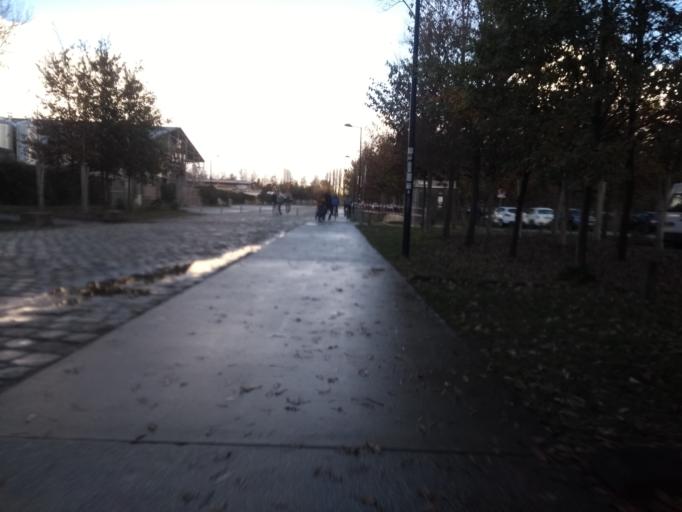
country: FR
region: Aquitaine
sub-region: Departement de la Gironde
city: Bordeaux
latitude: 44.8505
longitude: -0.5618
